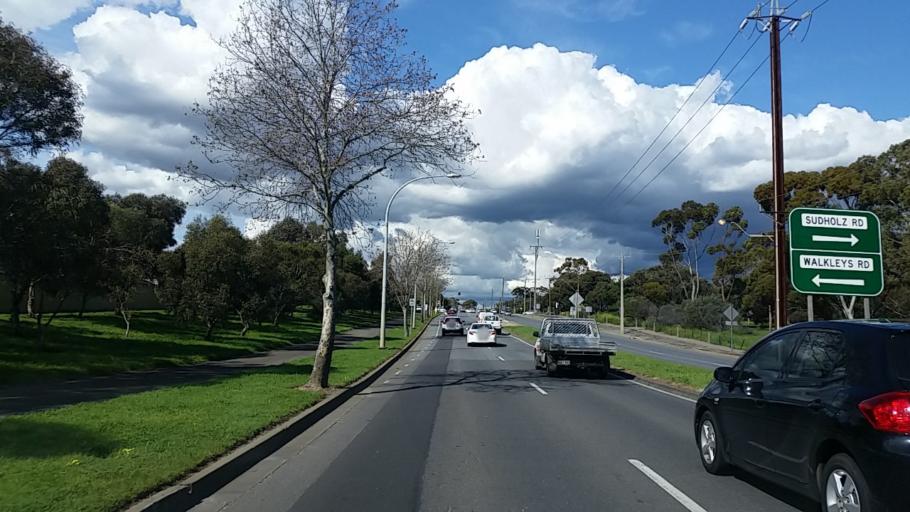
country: AU
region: South Australia
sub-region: Port Adelaide Enfield
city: Gilles Plains
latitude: -34.8462
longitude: 138.6461
